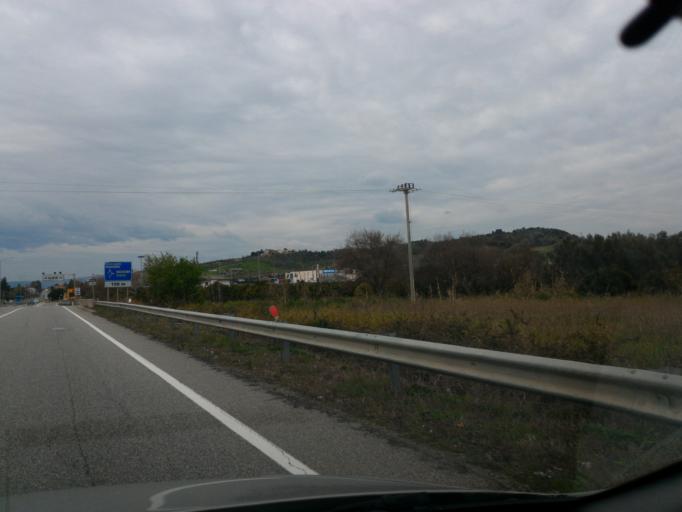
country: IT
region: Calabria
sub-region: Provincia di Catanzaro
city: Barone
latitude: 38.8443
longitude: 16.6527
